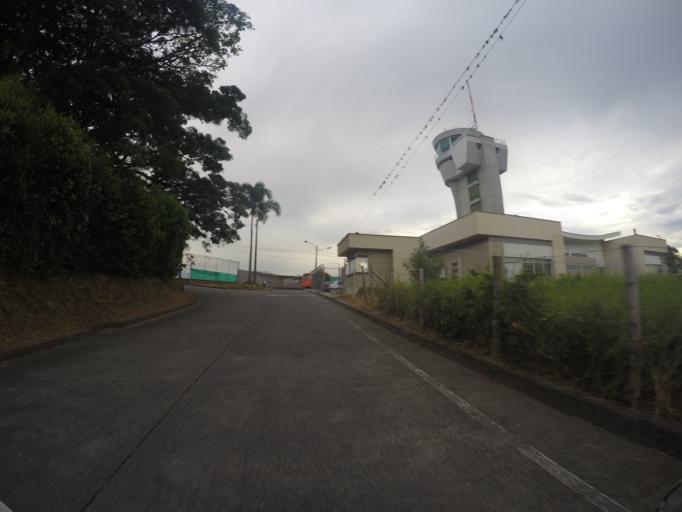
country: CO
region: Risaralda
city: Pereira
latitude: 4.8152
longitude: -75.7392
